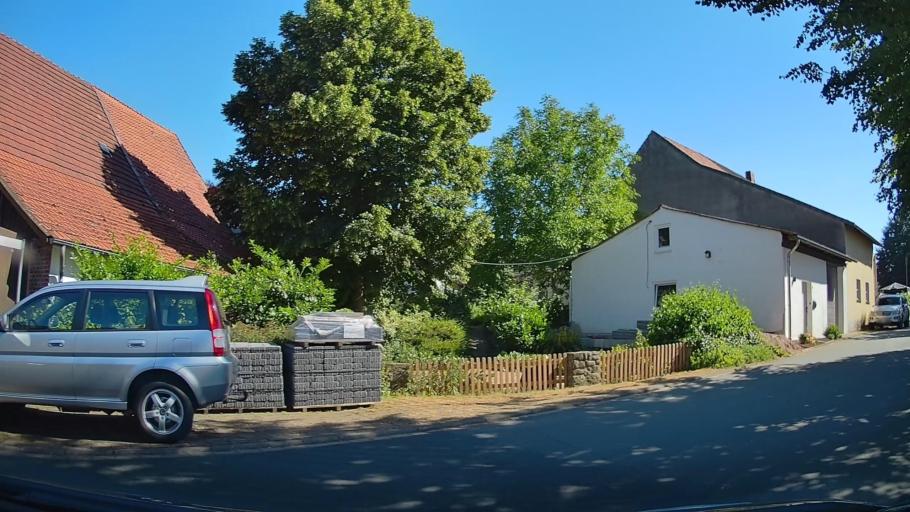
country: DE
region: Lower Saxony
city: Vahlbruch
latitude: 51.9696
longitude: 9.3551
